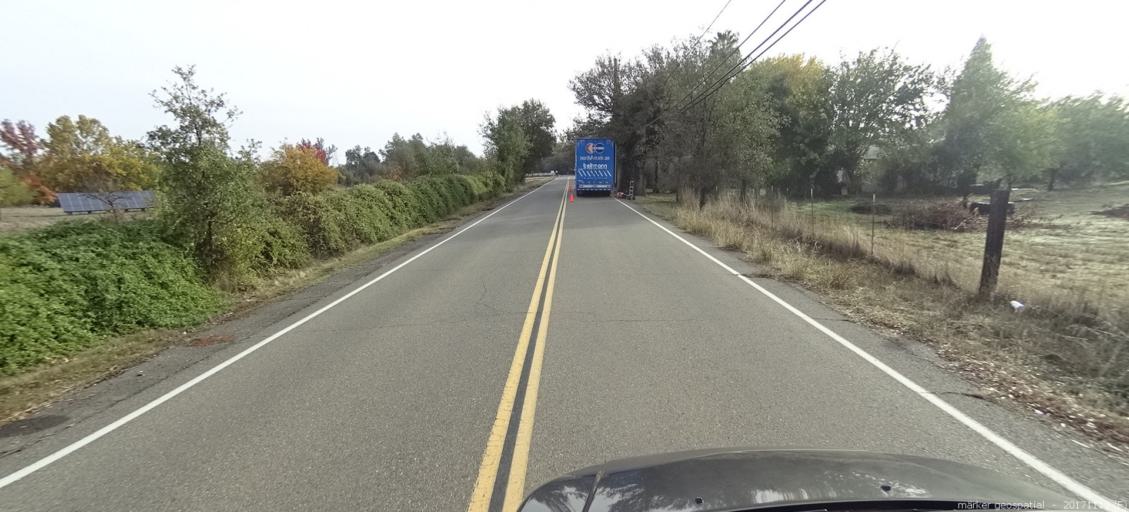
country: US
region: California
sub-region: Shasta County
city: Anderson
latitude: 40.5056
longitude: -122.3273
